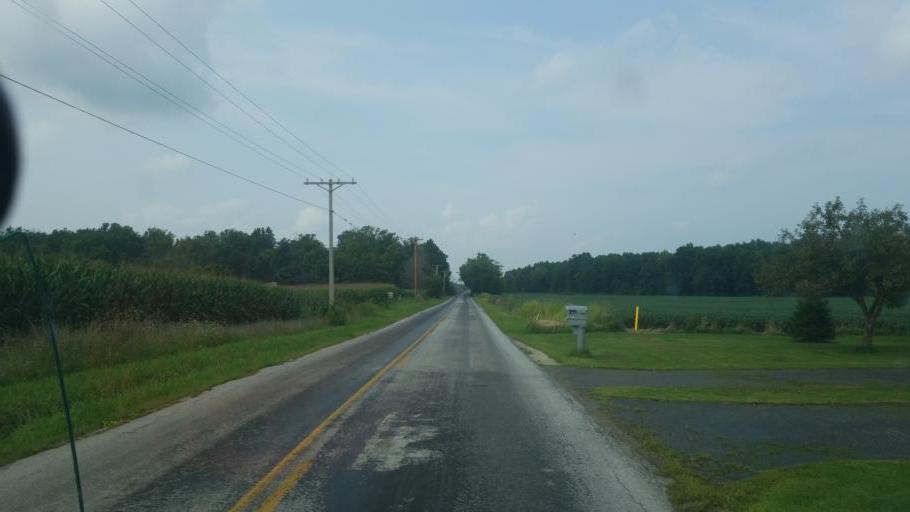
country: US
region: Ohio
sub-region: Lorain County
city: Wellington
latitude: 41.0764
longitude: -82.1619
